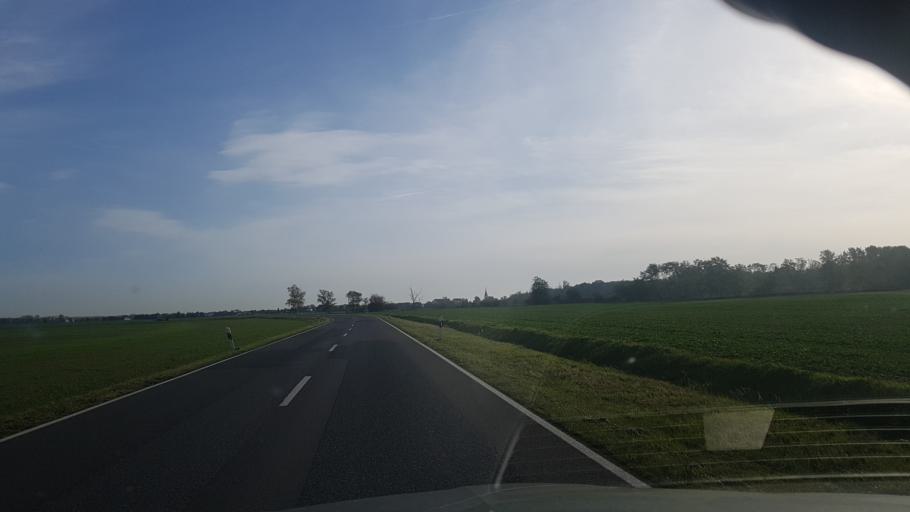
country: DE
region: Brandenburg
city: Grossthiemig
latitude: 51.3849
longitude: 13.6521
